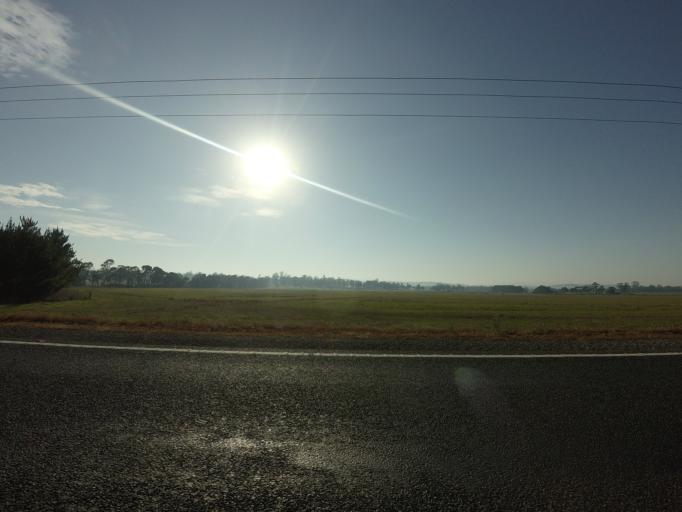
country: AU
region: Tasmania
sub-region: Northern Midlands
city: Longford
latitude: -41.5452
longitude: 147.0573
